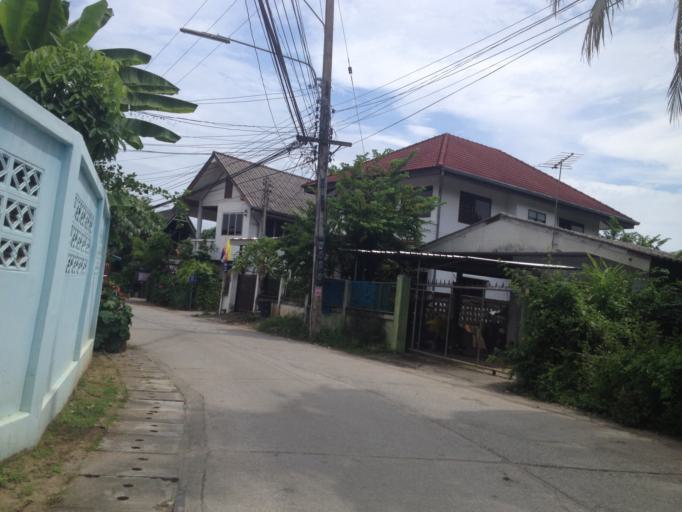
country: TH
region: Chiang Mai
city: Hang Dong
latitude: 18.7033
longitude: 98.9339
